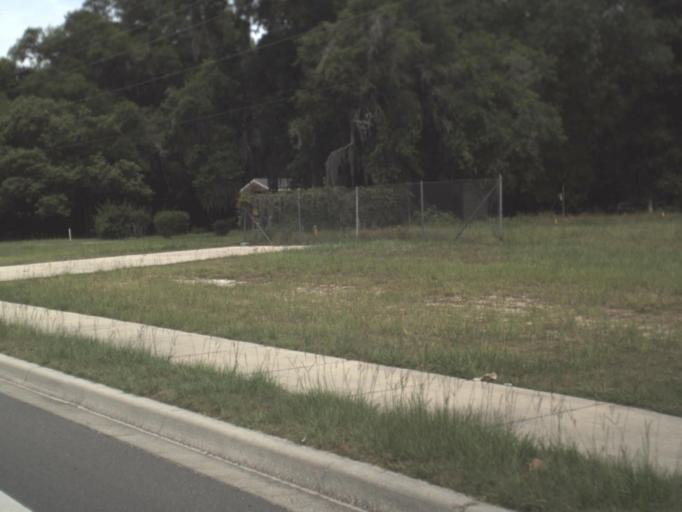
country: US
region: Florida
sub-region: Putnam County
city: Interlachen
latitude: 29.6289
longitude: -81.8821
